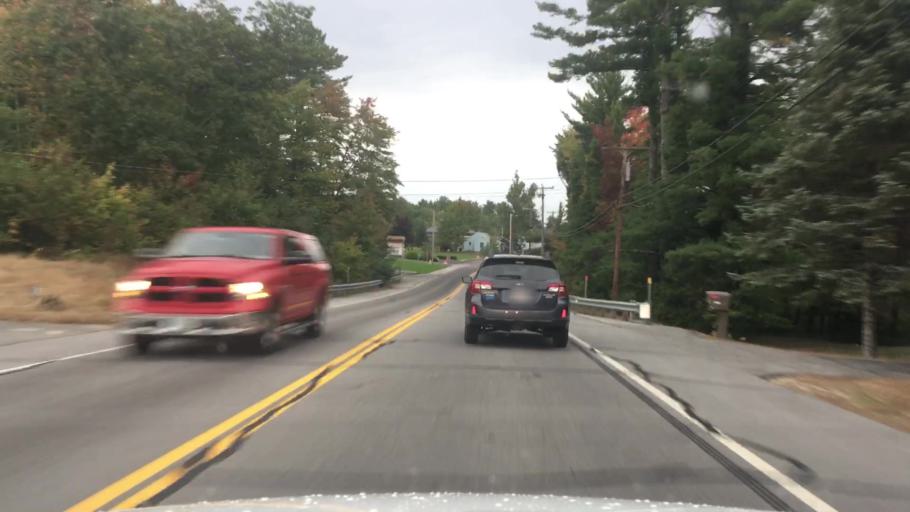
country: US
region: Maine
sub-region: York County
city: Waterboro
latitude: 43.5296
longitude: -70.7190
